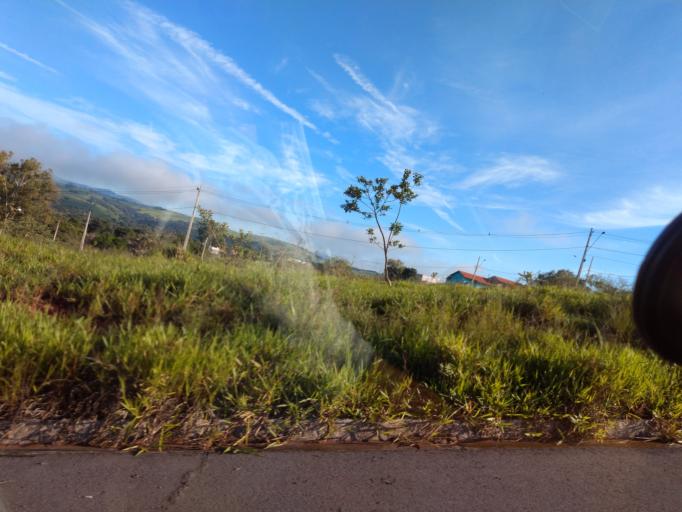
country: BR
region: Minas Gerais
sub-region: Tres Coracoes
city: Tres Coracoes
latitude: -21.6864
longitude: -45.2414
